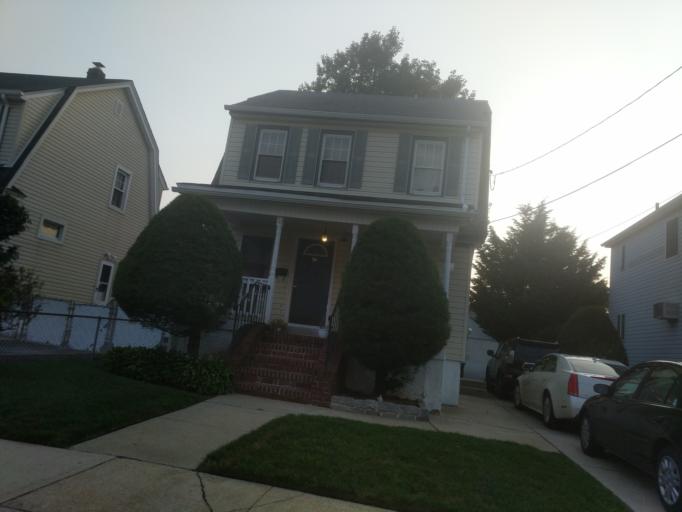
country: US
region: New York
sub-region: Nassau County
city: Valley Stream
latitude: 40.6595
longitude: -73.7059
